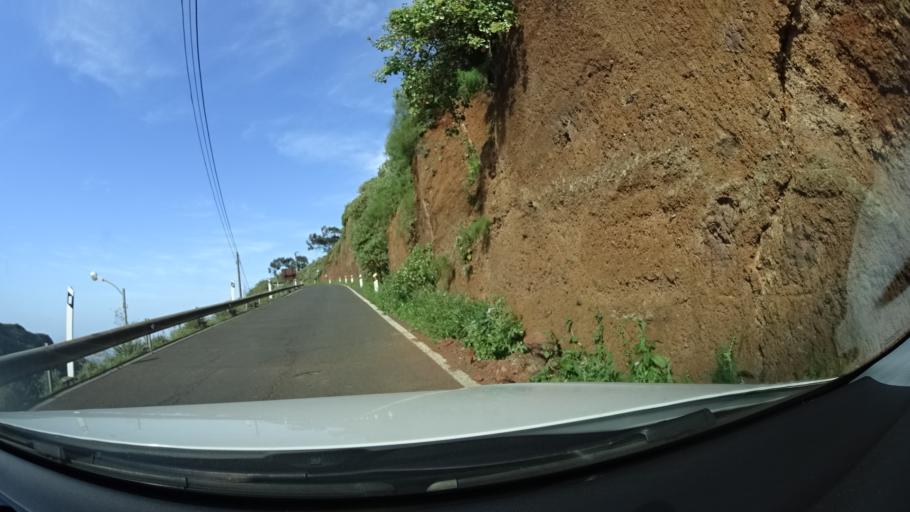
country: ES
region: Canary Islands
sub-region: Provincia de Las Palmas
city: Guia
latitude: 28.1097
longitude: -15.6391
